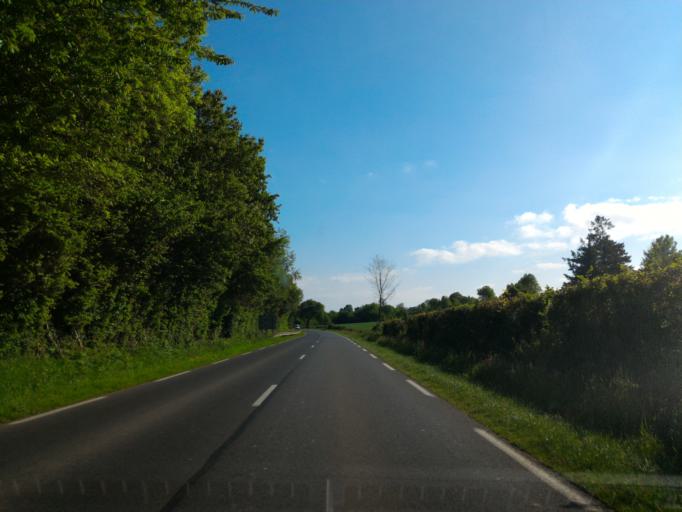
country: FR
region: Lower Normandy
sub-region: Departement de la Manche
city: La Haye-Pesnel
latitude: 48.8150
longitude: -1.3906
